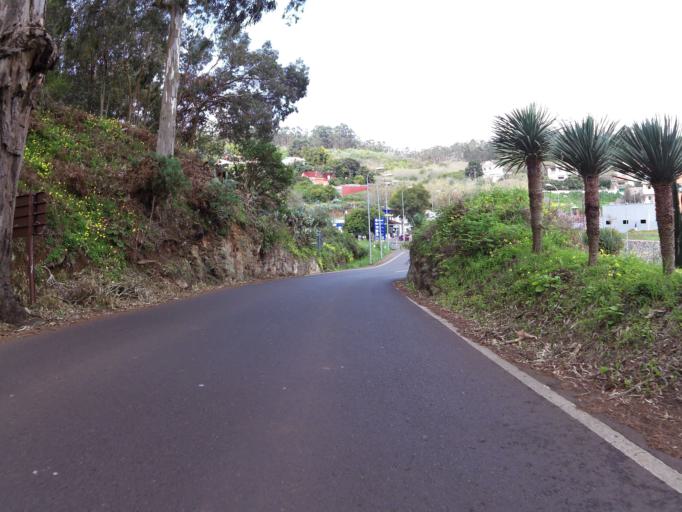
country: ES
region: Canary Islands
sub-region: Provincia de Las Palmas
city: Teror
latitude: 28.0861
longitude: -15.5413
